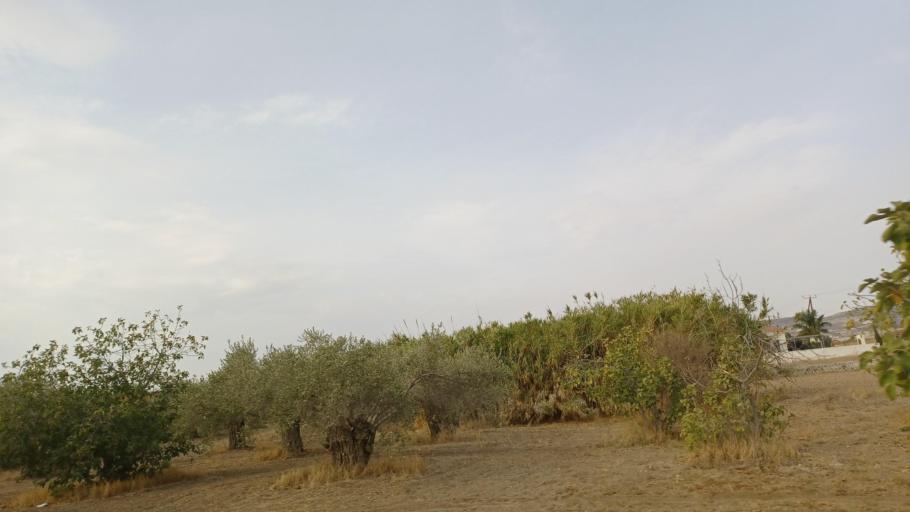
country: CY
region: Larnaka
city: Troulloi
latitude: 35.0276
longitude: 33.6059
